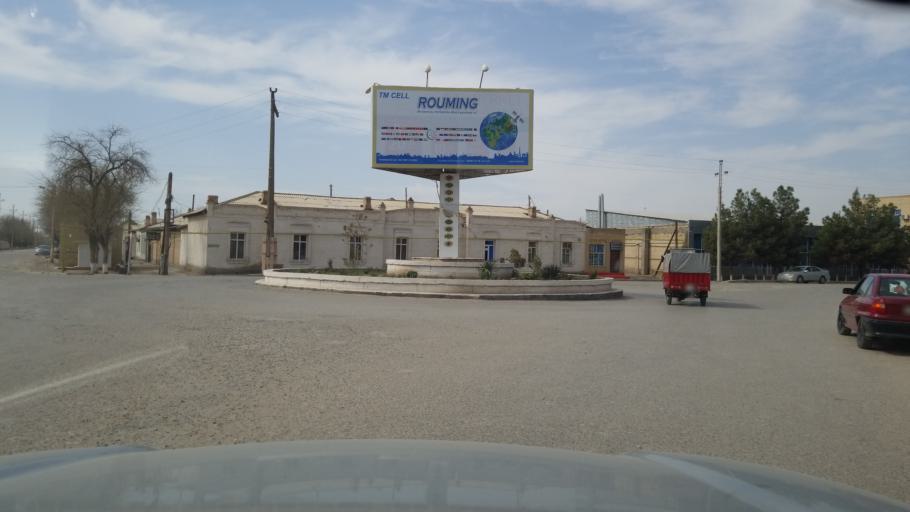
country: TM
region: Lebap
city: Atamyrat
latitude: 37.8348
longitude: 65.2120
